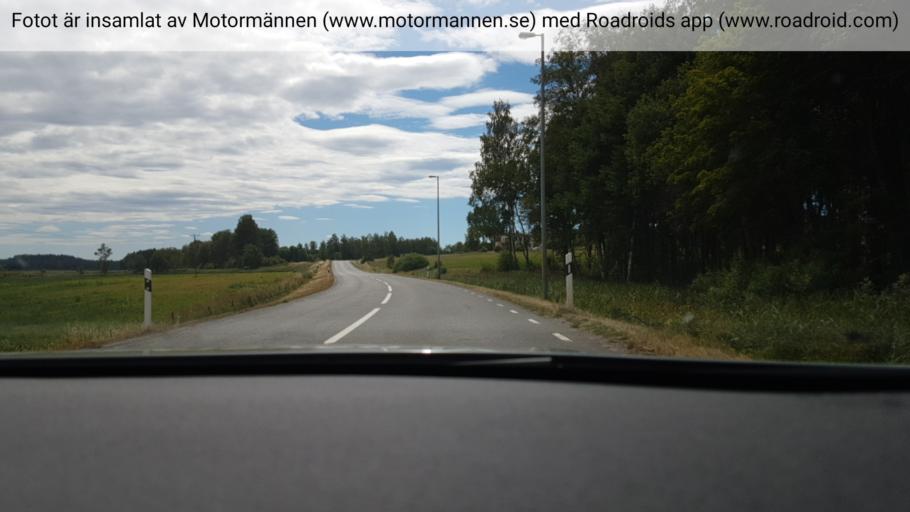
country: SE
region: Joenkoeping
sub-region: Tranas Kommun
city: Tranas
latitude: 57.9885
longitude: 14.8429
